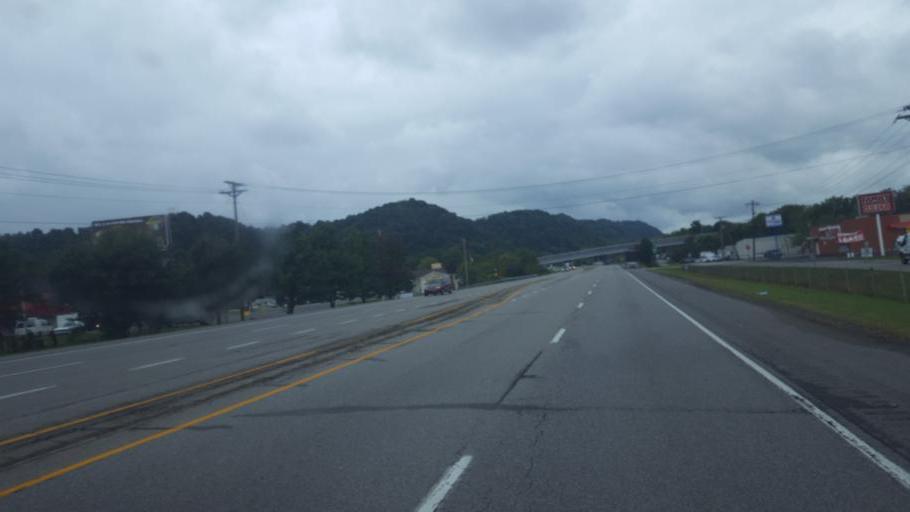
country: US
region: Kentucky
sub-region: Greenup County
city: South Shore
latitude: 38.7210
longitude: -82.9590
